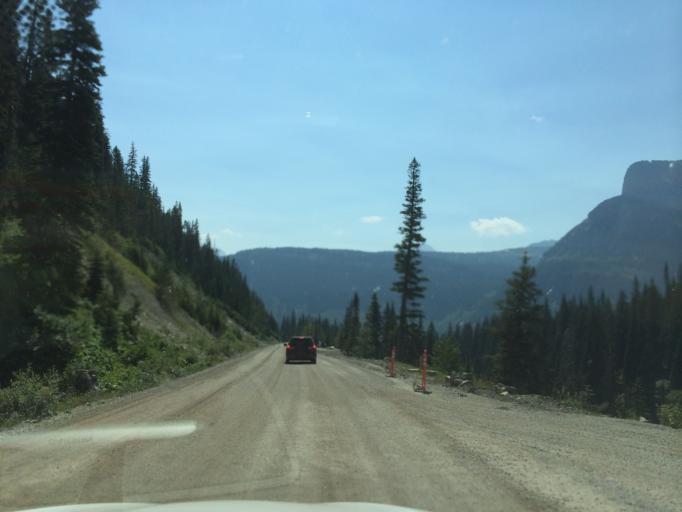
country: US
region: Montana
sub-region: Flathead County
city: Columbia Falls
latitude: 48.6954
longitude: -113.6680
